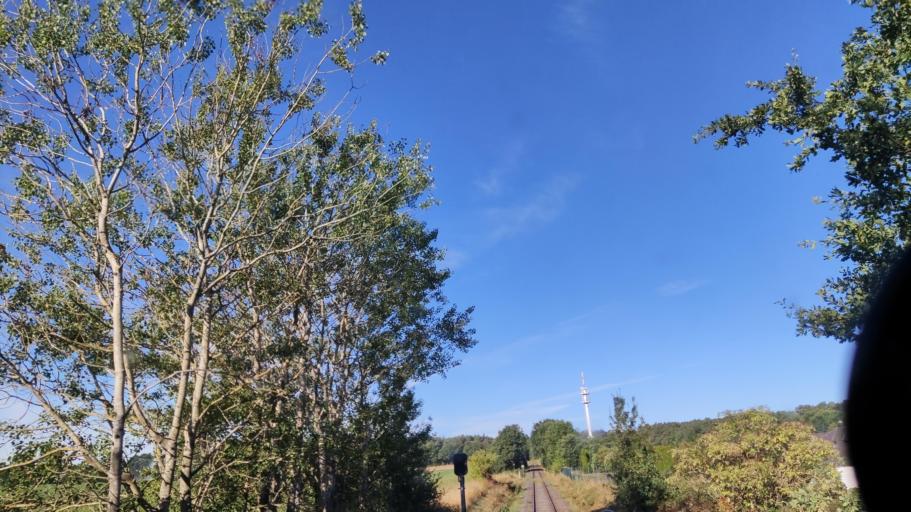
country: DE
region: Lower Saxony
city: Betzendorf
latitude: 53.1469
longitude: 10.2966
